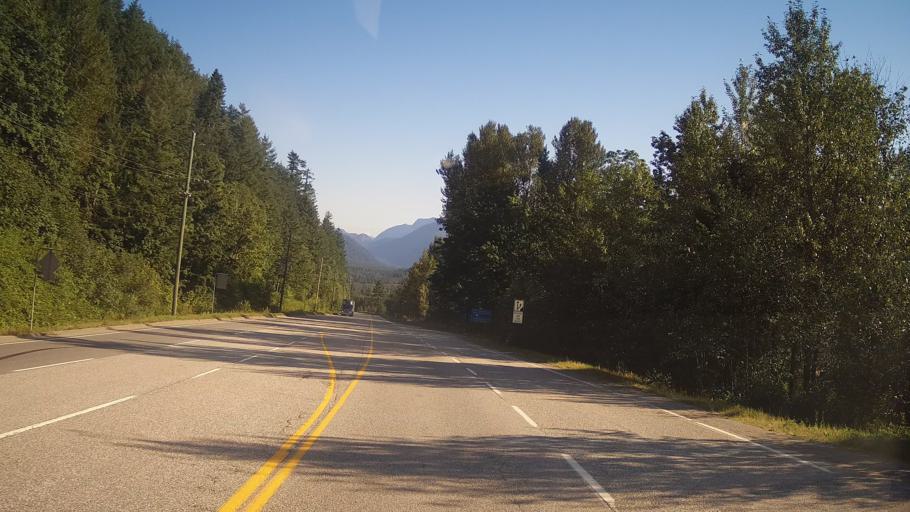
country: CA
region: British Columbia
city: Hope
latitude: 49.4157
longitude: -121.4375
